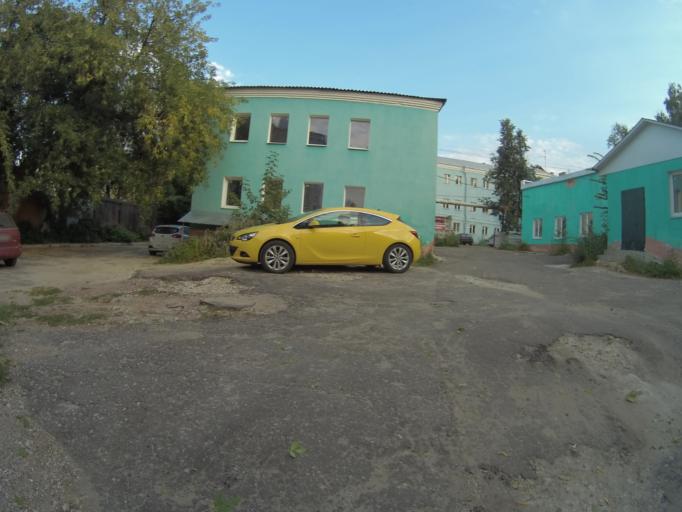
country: RU
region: Vladimir
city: Vladimir
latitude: 56.1325
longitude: 40.4128
